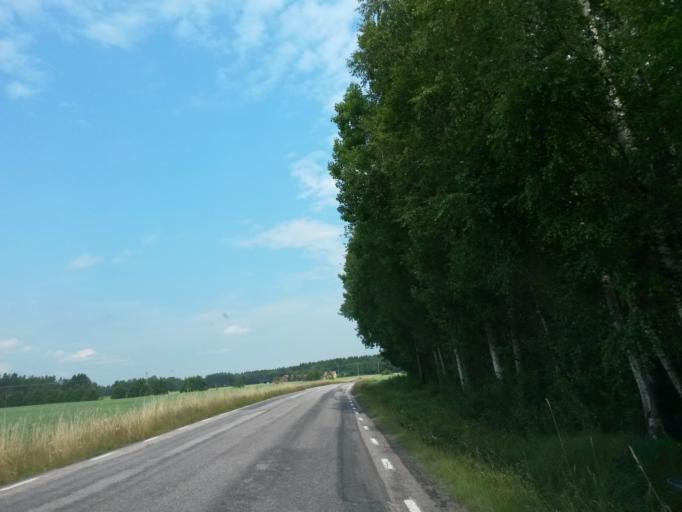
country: SE
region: Vaestra Goetaland
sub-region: Essunga Kommun
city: Nossebro
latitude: 58.1571
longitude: 12.7474
